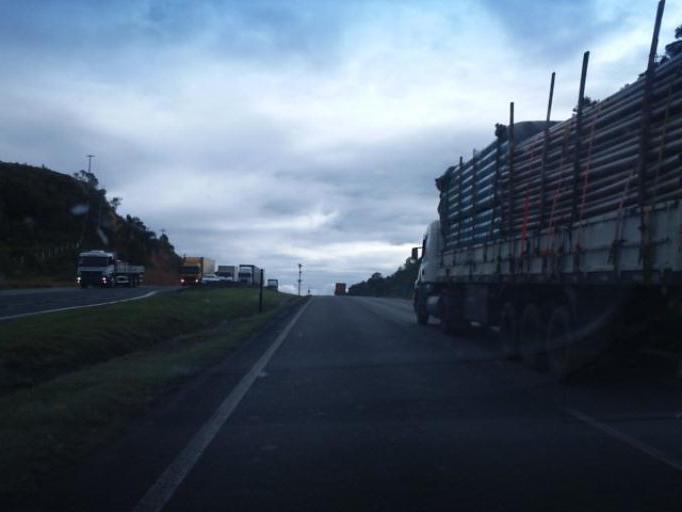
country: BR
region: Parana
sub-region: Campina Grande Do Sul
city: Campina Grande do Sul
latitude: -25.2698
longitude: -48.9189
